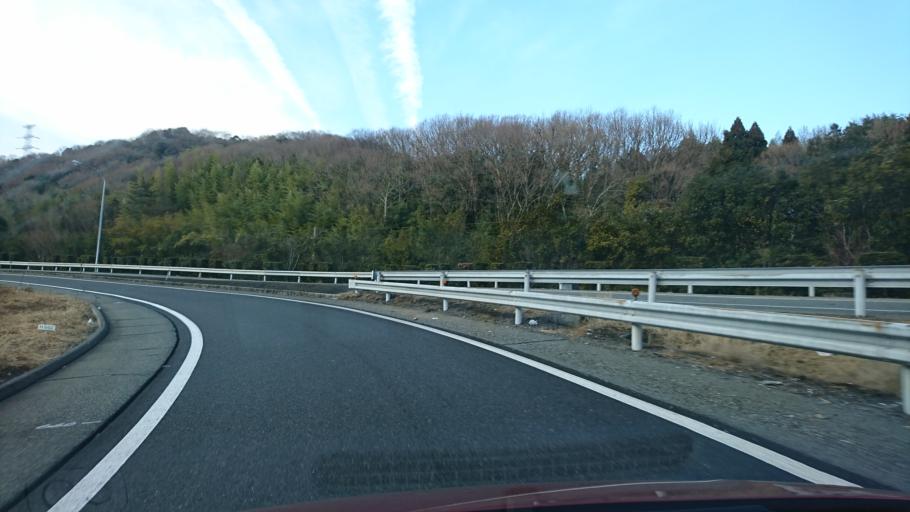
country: JP
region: Hyogo
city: Himeji
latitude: 34.8571
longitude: 134.7370
